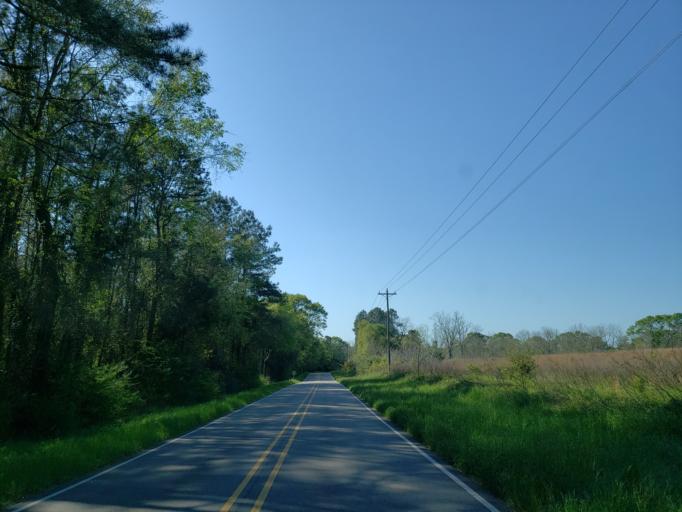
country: US
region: Mississippi
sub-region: Jones County
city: Ellisville
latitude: 31.5804
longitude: -89.3753
